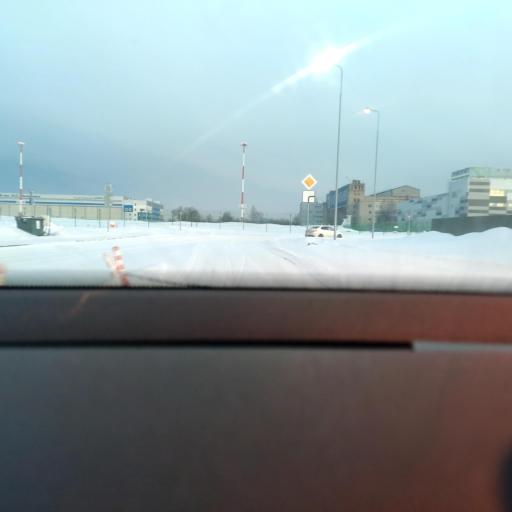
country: RU
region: Moskovskaya
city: Zhukovskiy
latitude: 55.5596
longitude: 38.1193
